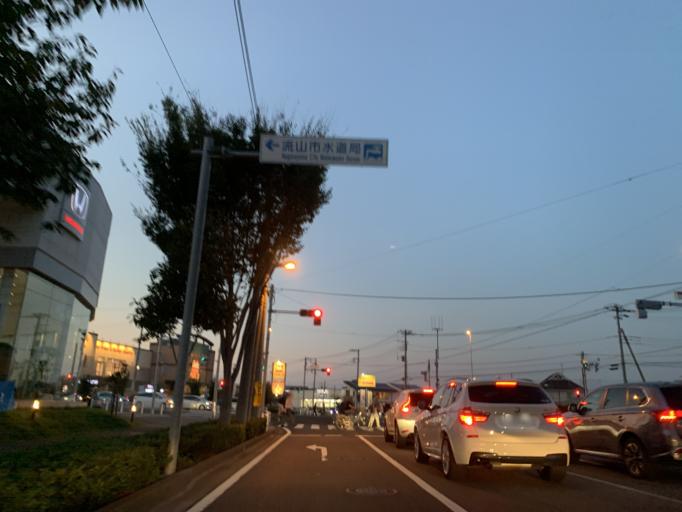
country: JP
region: Chiba
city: Nagareyama
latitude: 35.8729
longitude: 139.9200
